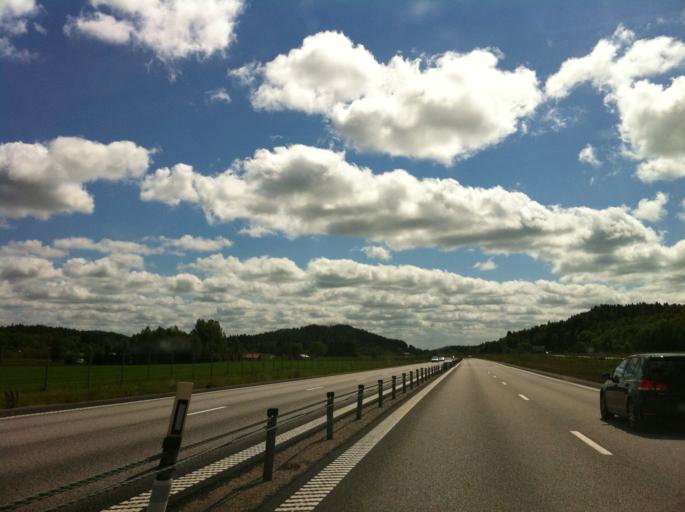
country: SE
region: Vaestra Goetaland
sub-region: Lilla Edets Kommun
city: Lodose
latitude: 58.0814
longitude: 12.1568
